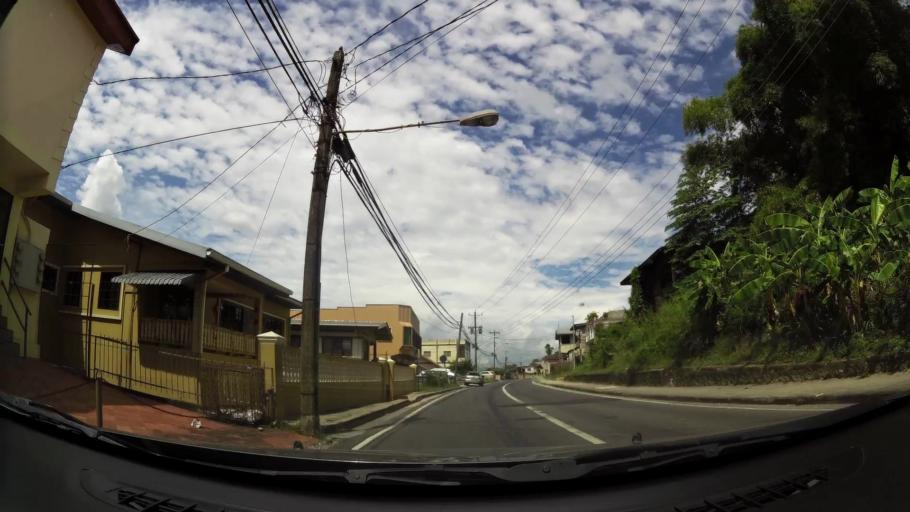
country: TT
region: City of San Fernando
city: San Fernando
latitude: 10.2894
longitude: -61.4561
